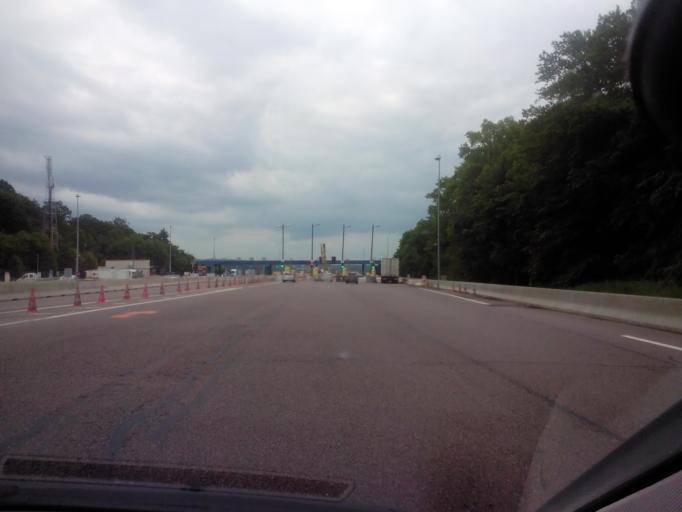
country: FR
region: Lorraine
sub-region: Departement de la Moselle
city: Farschviller
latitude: 49.0761
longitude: 6.8936
